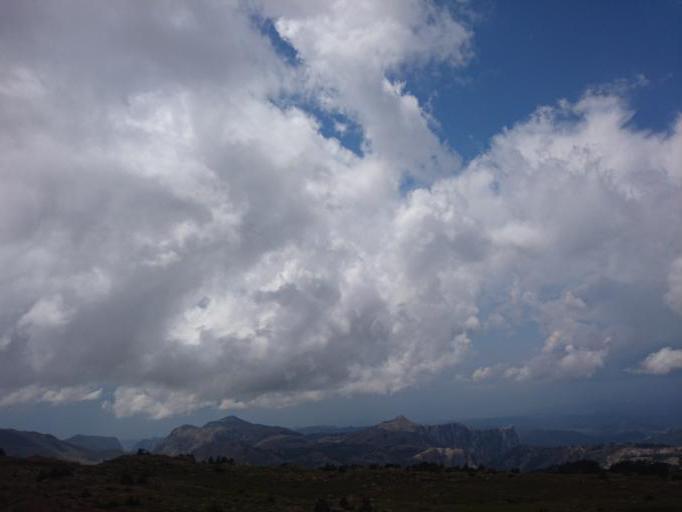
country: AL
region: Diber
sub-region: Rrethi i Dibres
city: Fushe-Lure
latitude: 41.7851
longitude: 20.1781
